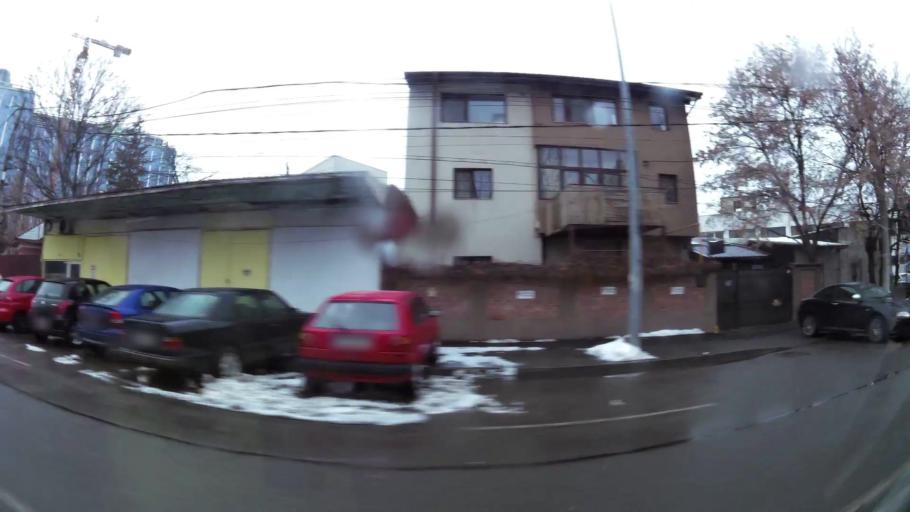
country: RO
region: Ilfov
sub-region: Comuna Chiajna
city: Rosu
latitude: 44.4722
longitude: 26.0561
